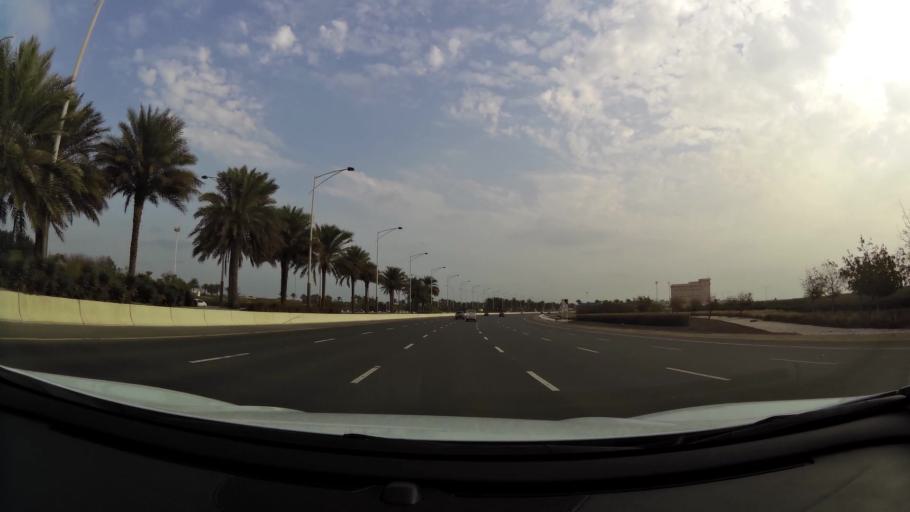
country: AE
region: Abu Dhabi
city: Abu Dhabi
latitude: 24.5381
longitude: 54.4369
